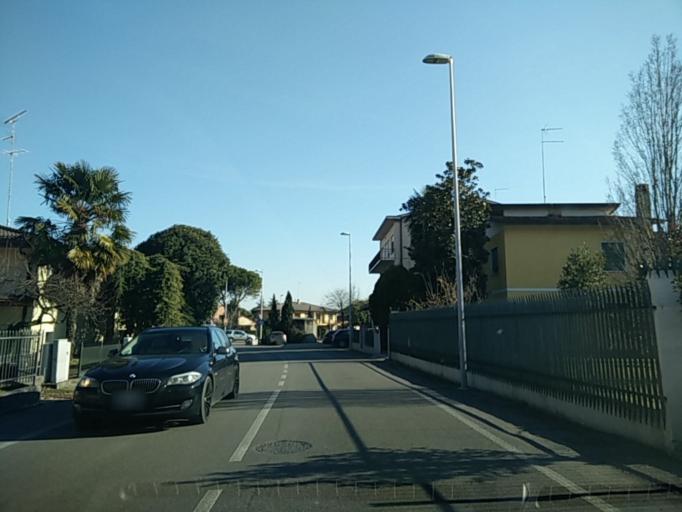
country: IT
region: Veneto
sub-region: Provincia di Treviso
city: Cosniga-Zoppe
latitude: 45.8876
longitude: 12.3591
